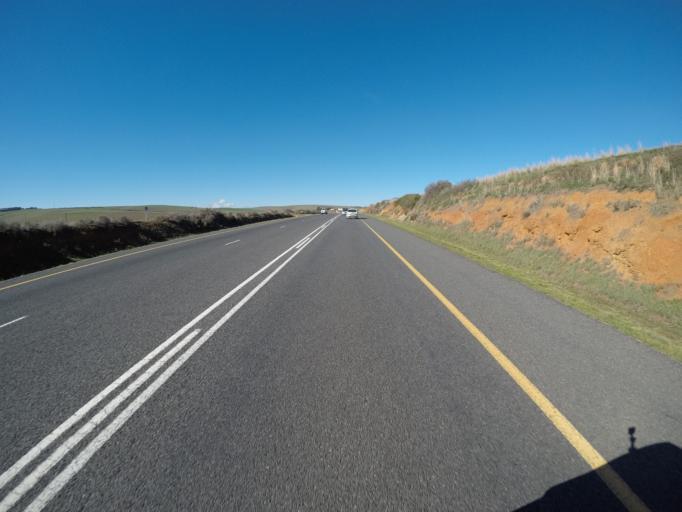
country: ZA
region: Western Cape
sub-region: Overberg District Municipality
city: Caledon
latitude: -34.2333
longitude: 19.2463
